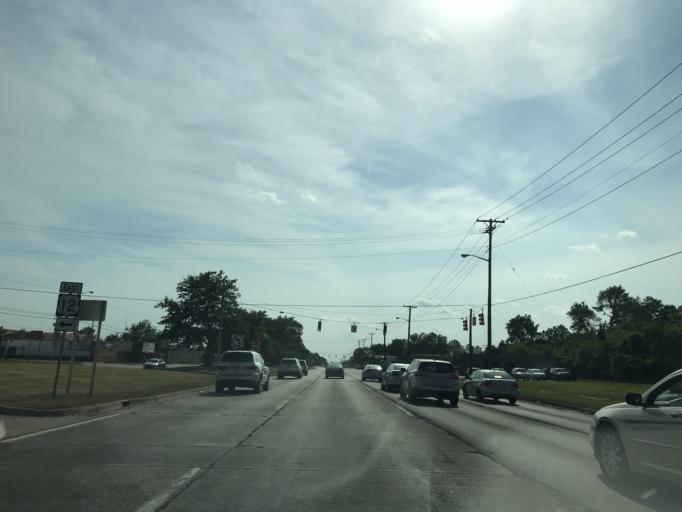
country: US
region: Michigan
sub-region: Wayne County
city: Inkster
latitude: 42.2905
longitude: -83.3258
